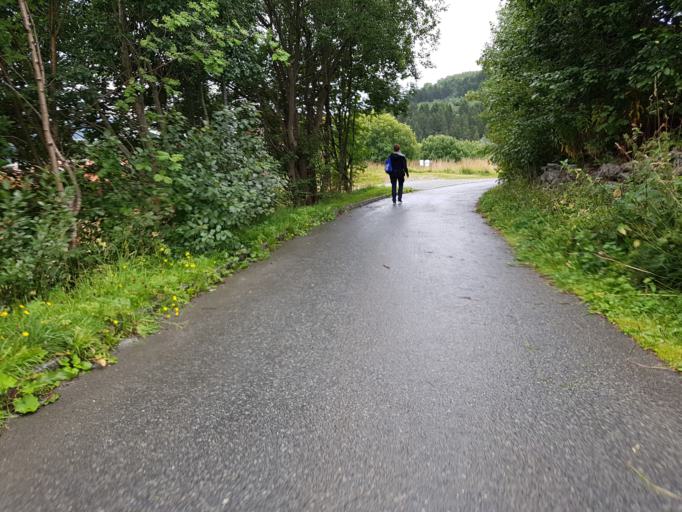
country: NO
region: Sor-Trondelag
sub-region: Trondheim
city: Trondheim
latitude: 63.3858
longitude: 10.3381
